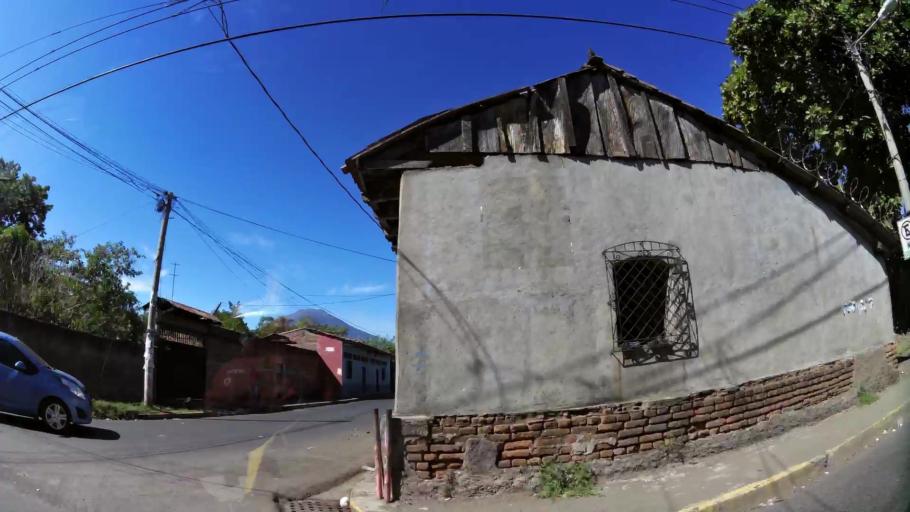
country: SV
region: San Miguel
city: San Miguel
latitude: 13.4857
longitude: -88.1709
